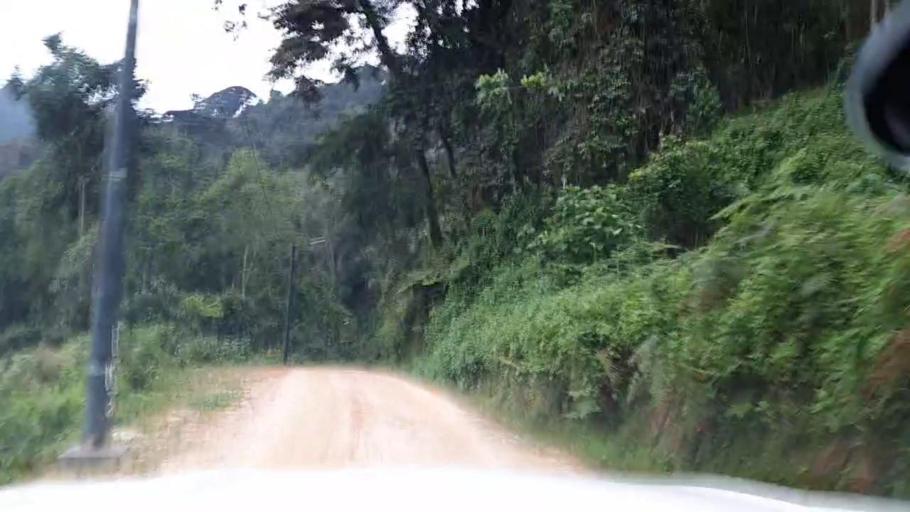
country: RW
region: Western Province
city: Cyangugu
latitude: -2.5677
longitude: 29.2307
